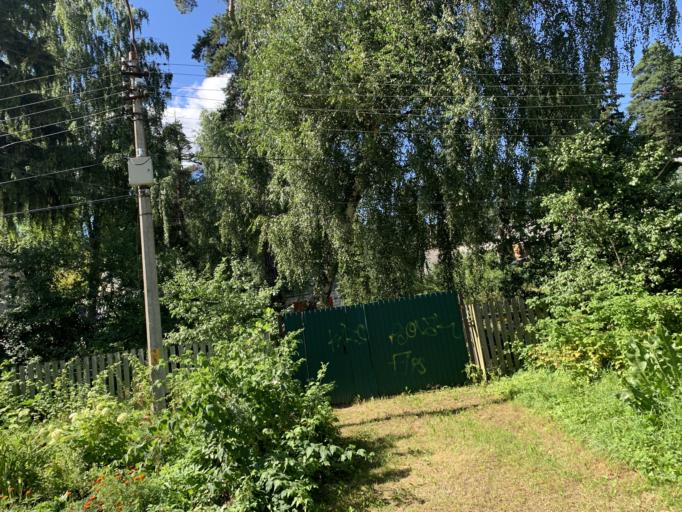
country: RU
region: Moskovskaya
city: Mamontovka
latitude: 55.9787
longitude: 37.8269
